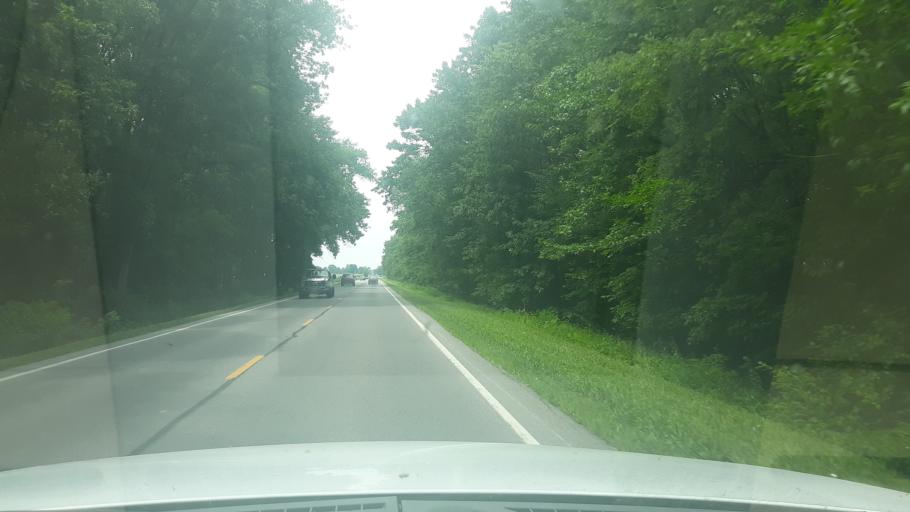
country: US
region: Illinois
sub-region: Saline County
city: Harrisburg
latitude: 37.7811
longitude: -88.5401
